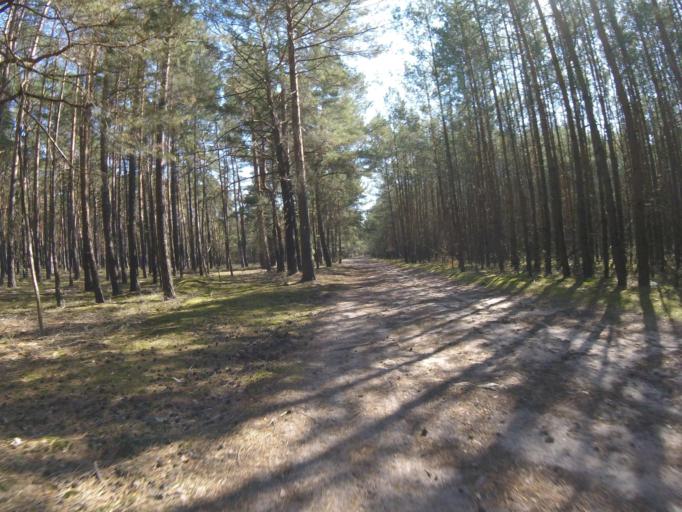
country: DE
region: Brandenburg
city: Bestensee
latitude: 52.2643
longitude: 13.6837
